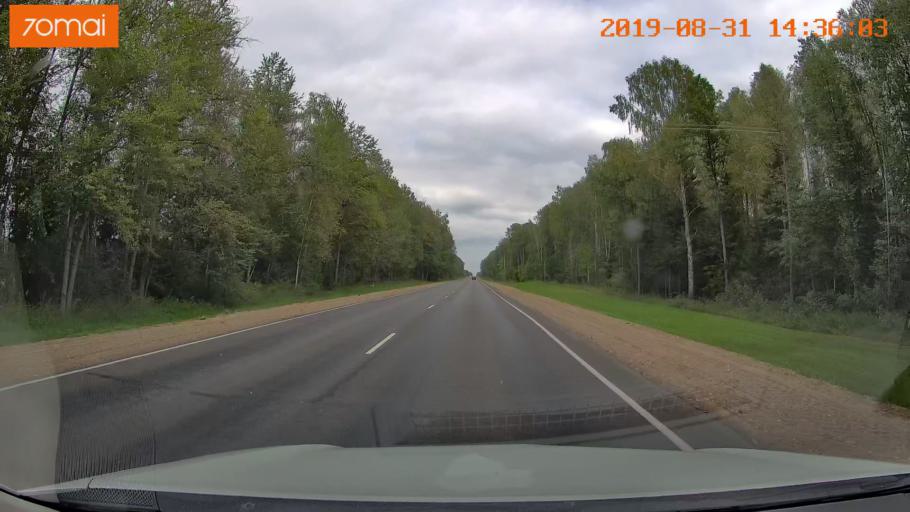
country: RU
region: Smolensk
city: Yekimovichi
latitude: 54.1671
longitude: 33.4700
